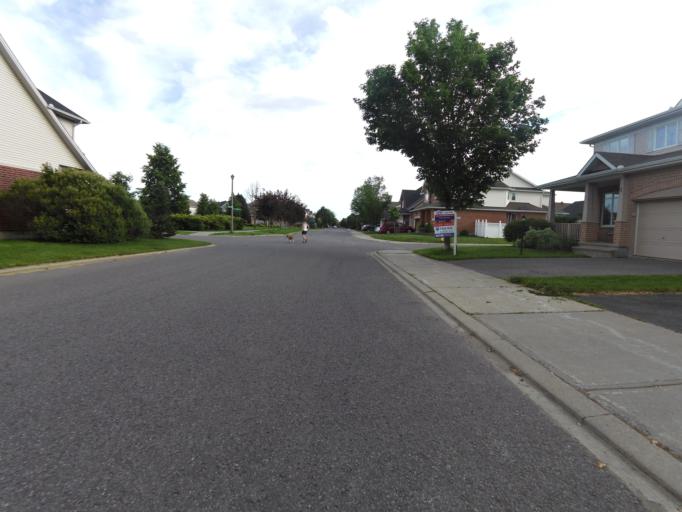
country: CA
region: Ontario
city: Ottawa
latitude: 45.2888
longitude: -75.7073
